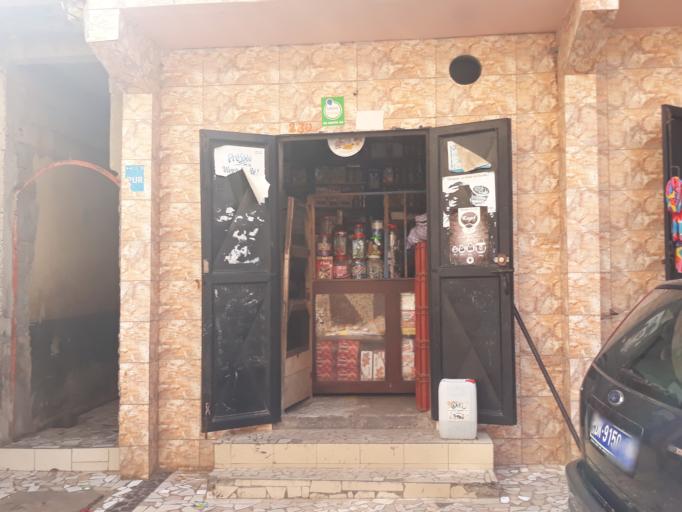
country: SN
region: Dakar
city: Dakar
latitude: 14.6895
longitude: -17.4493
